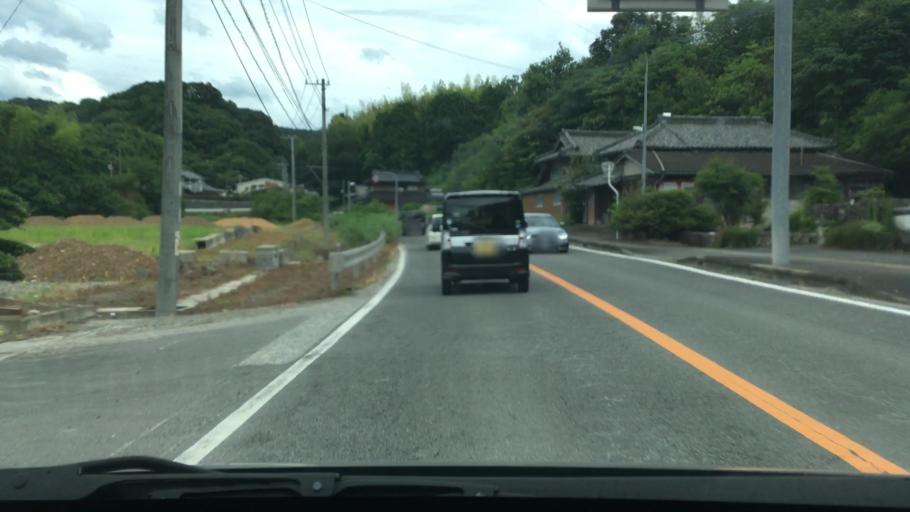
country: JP
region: Nagasaki
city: Togitsu
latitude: 32.9841
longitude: 129.7790
